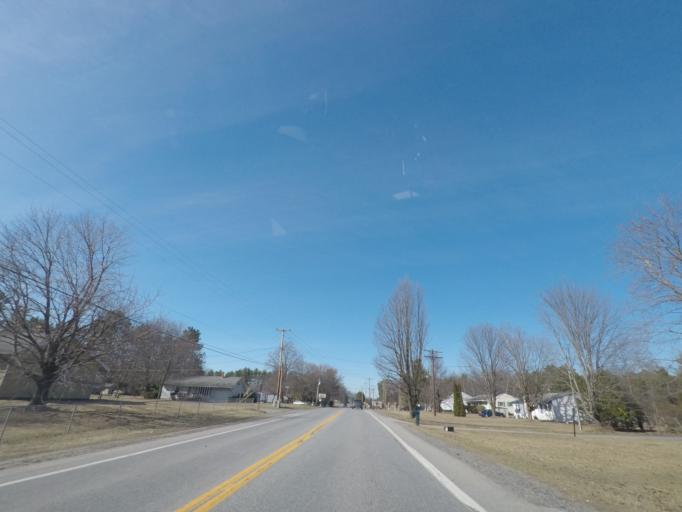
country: US
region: New York
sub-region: Saratoga County
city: Milton
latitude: 43.0403
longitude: -73.8497
